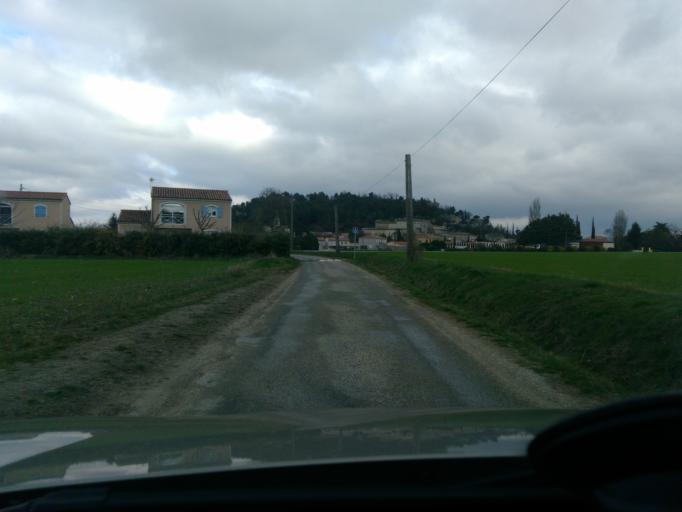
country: FR
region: Rhone-Alpes
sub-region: Departement de la Drome
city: Montboucher-sur-Jabron
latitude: 44.5494
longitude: 4.8641
